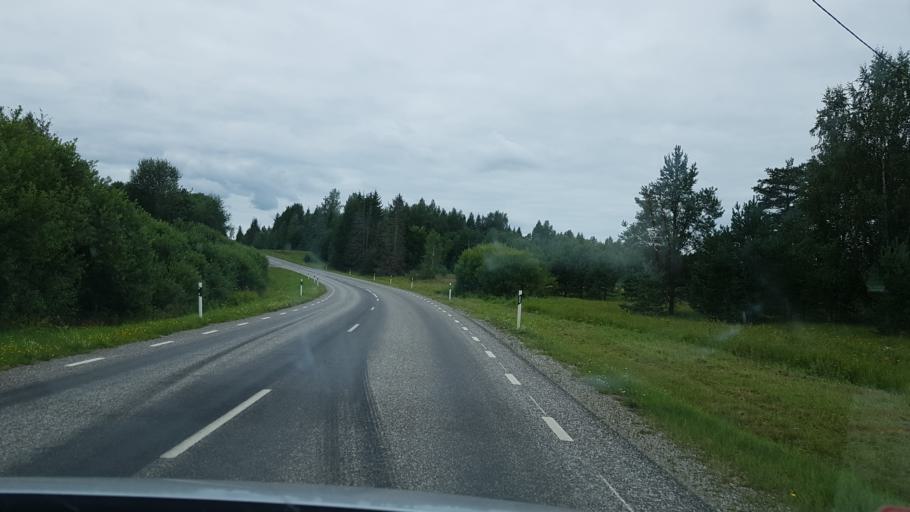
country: EE
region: Vorumaa
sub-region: Antsla vald
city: Vana-Antsla
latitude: 57.9947
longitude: 26.7371
